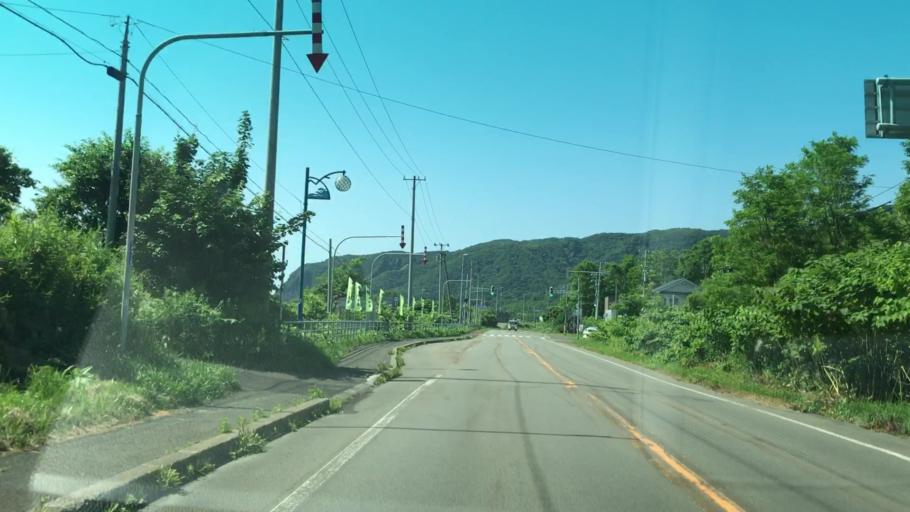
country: JP
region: Hokkaido
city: Iwanai
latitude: 43.0700
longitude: 140.4917
